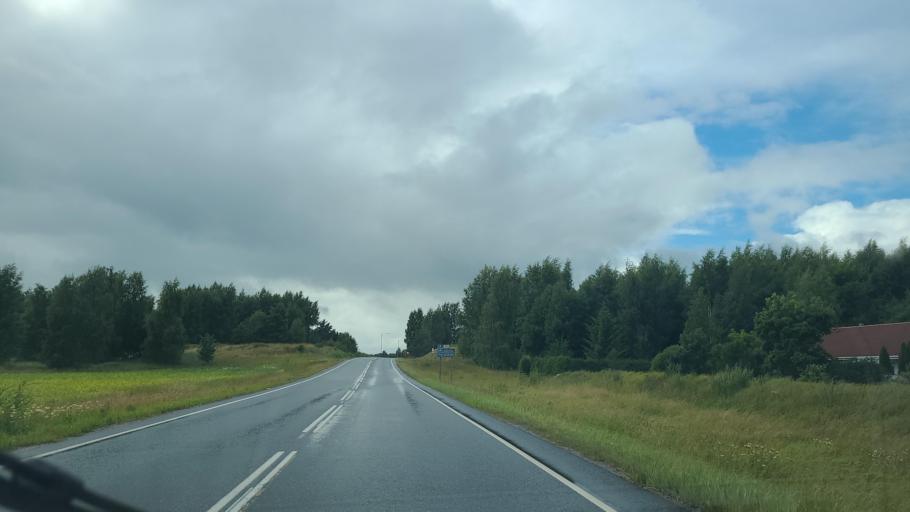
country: FI
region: Varsinais-Suomi
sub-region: Turku
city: Sauvo
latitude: 60.3402
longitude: 22.6964
